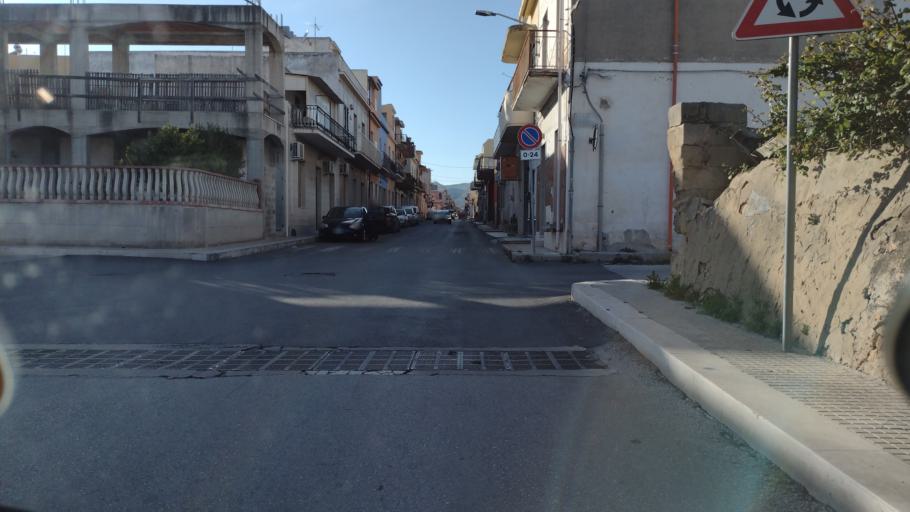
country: IT
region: Sicily
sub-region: Provincia di Siracusa
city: Avola
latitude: 36.9025
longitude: 15.1389
